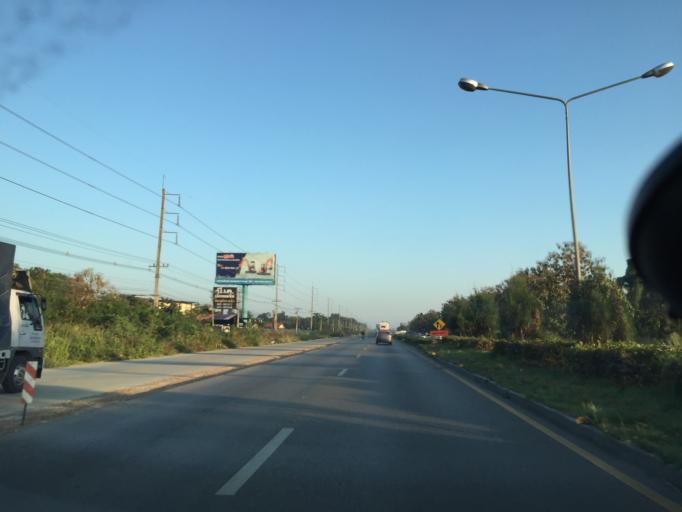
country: TH
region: Chiang Mai
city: Saraphi
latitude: 18.6822
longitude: 99.0503
